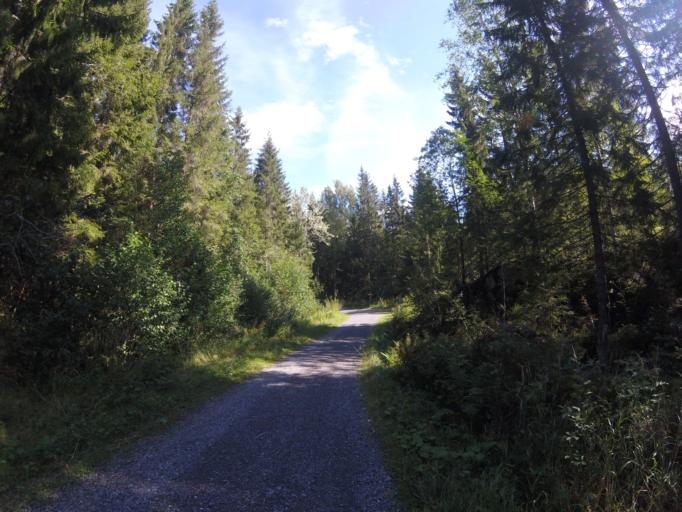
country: NO
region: Akershus
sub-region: Lorenskog
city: Kjenn
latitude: 59.8481
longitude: 11.0055
